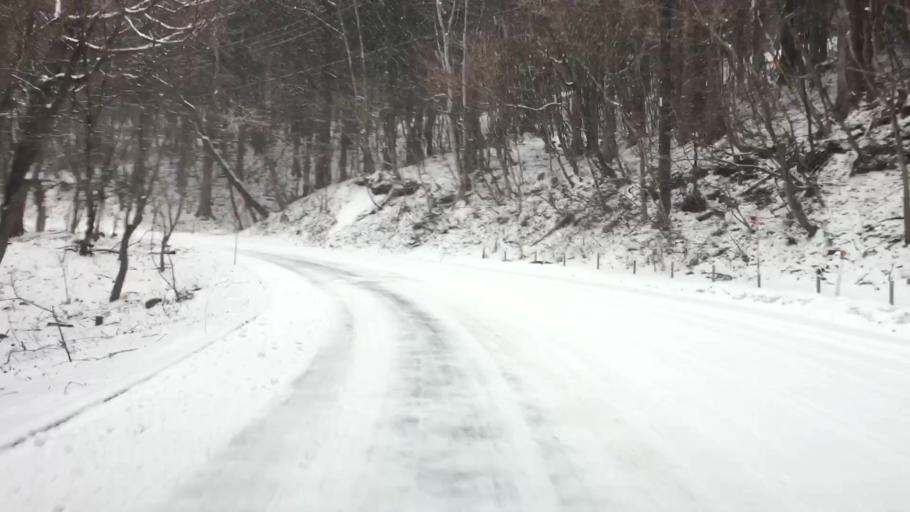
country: JP
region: Tochigi
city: Imaichi
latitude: 36.8812
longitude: 139.7310
